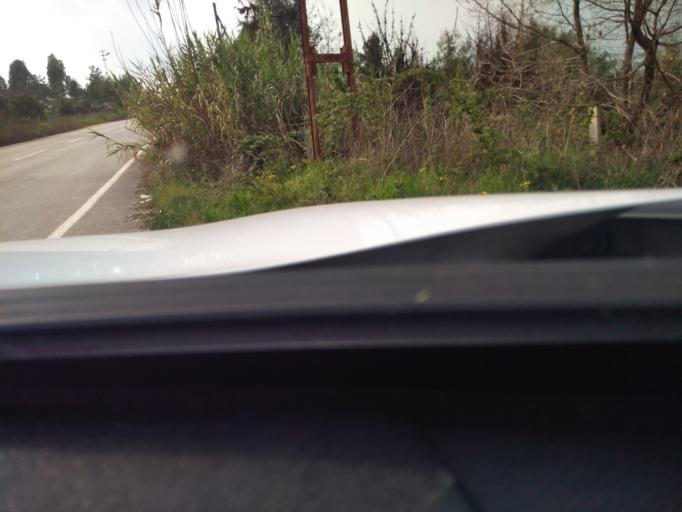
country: TR
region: Adana
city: Adana
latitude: 37.0662
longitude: 35.2785
